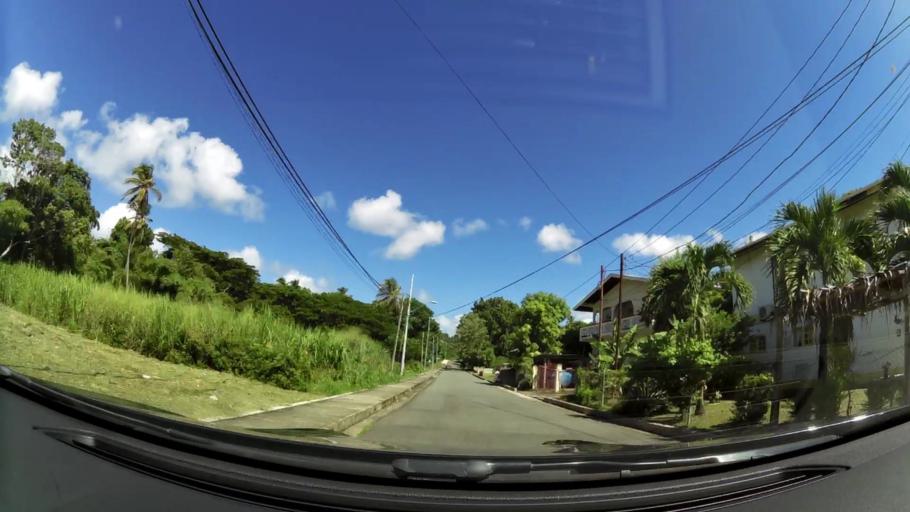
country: TT
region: Tobago
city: Scarborough
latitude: 11.1724
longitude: -60.7819
